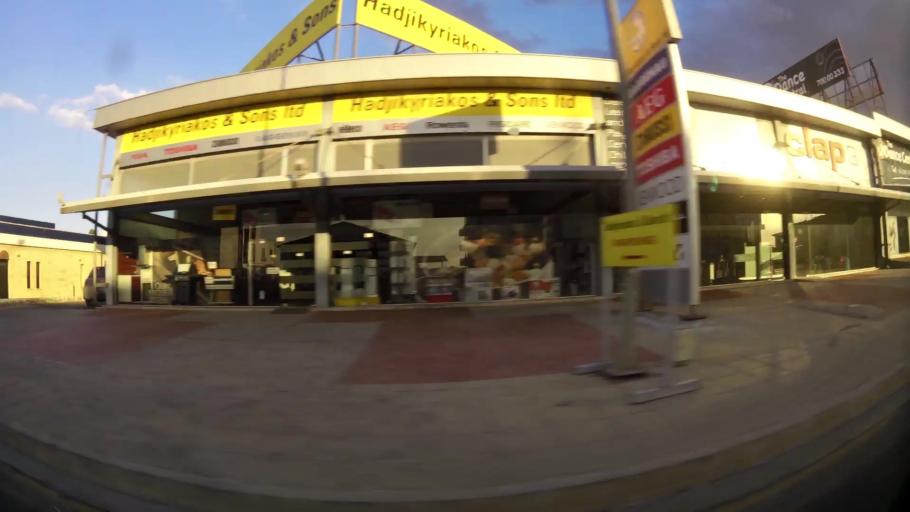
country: CY
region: Lefkosia
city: Tseri
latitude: 35.1280
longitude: 33.3247
